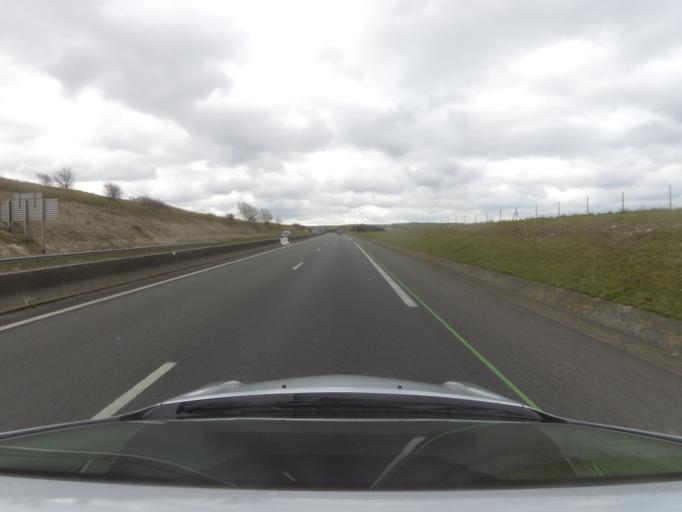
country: FR
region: Nord-Pas-de-Calais
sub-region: Departement du Pas-de-Calais
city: Nesles
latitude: 50.6209
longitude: 1.6590
